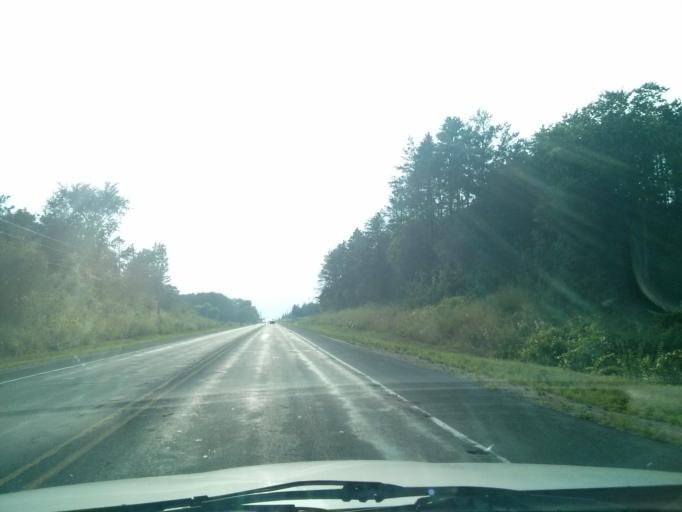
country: US
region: Wisconsin
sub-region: Saint Croix County
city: Hudson
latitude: 44.9780
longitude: -92.7106
